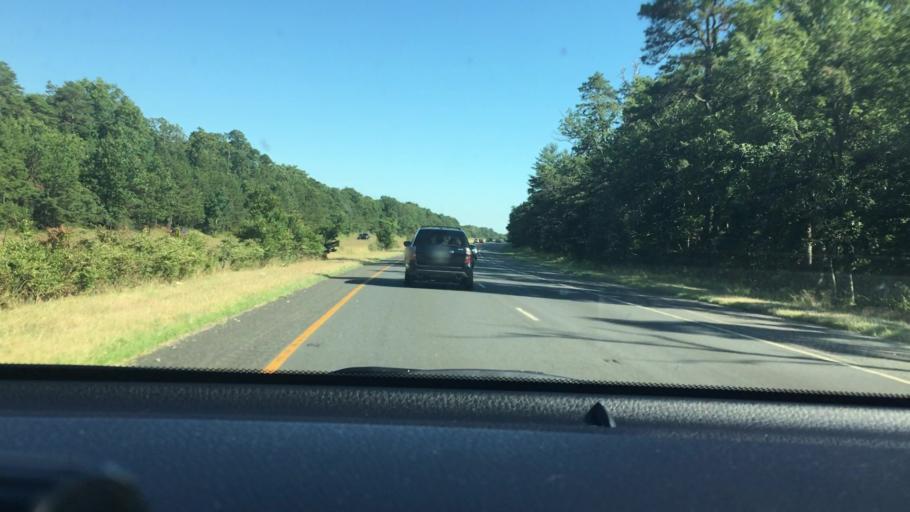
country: US
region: New Jersey
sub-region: Gloucester County
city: Newfield
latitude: 39.5666
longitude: -75.0617
